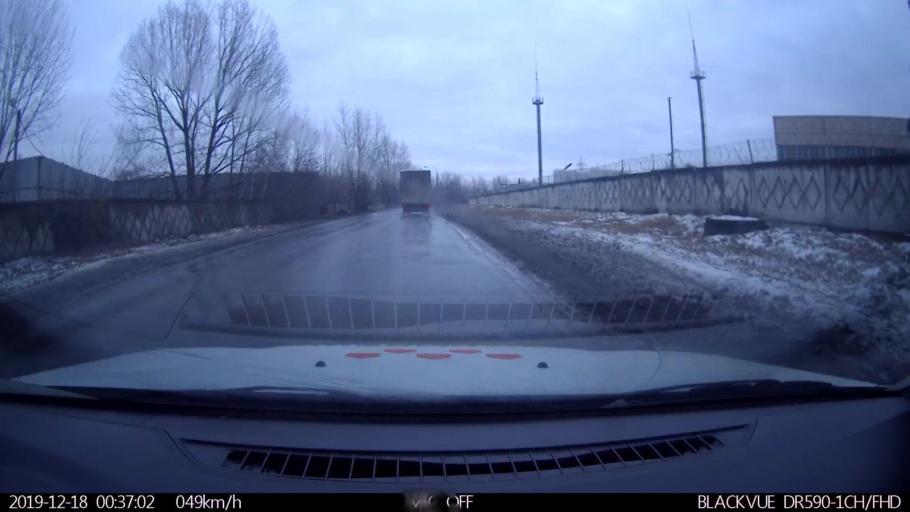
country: RU
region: Nizjnij Novgorod
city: Neklyudovo
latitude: 56.3554
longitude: 43.8937
